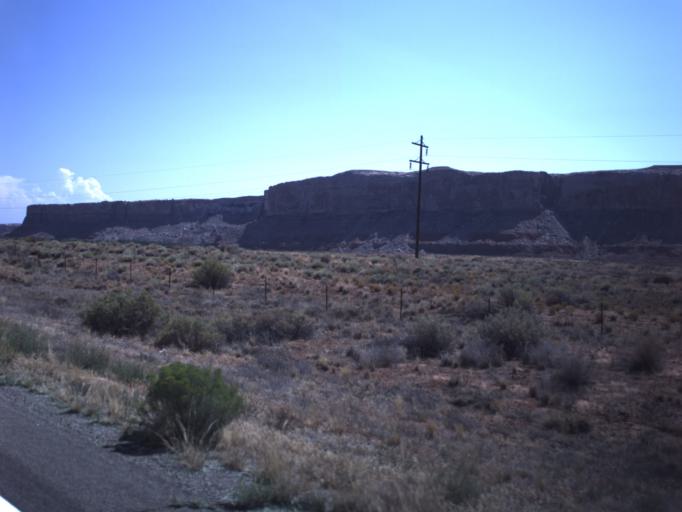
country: US
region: Utah
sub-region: San Juan County
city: Blanding
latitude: 37.2696
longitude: -109.6000
